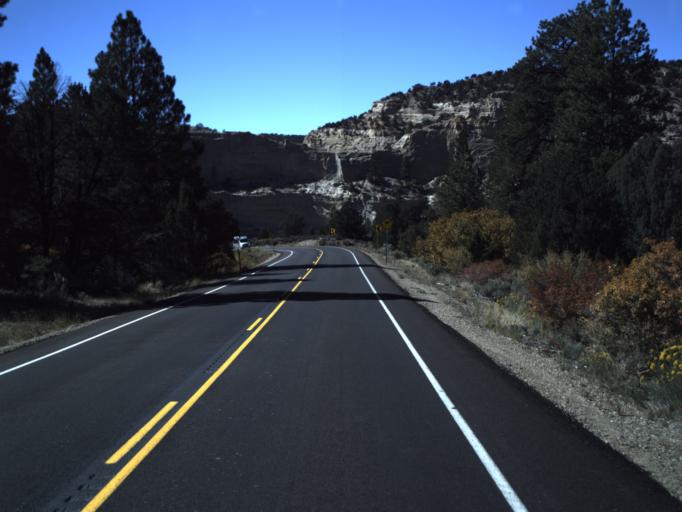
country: US
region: Utah
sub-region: Garfield County
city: Panguitch
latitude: 37.6164
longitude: -111.8907
